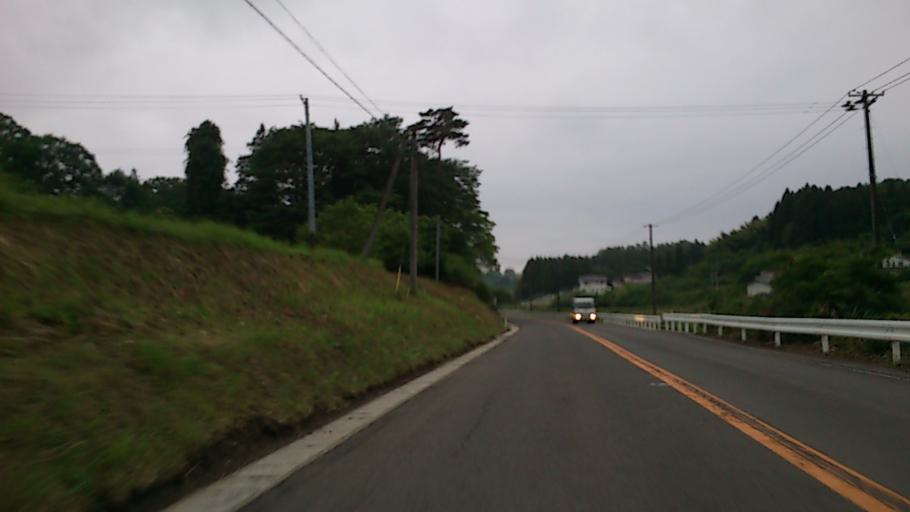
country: JP
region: Fukushima
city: Fukushima-shi
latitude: 37.6792
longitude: 140.5275
